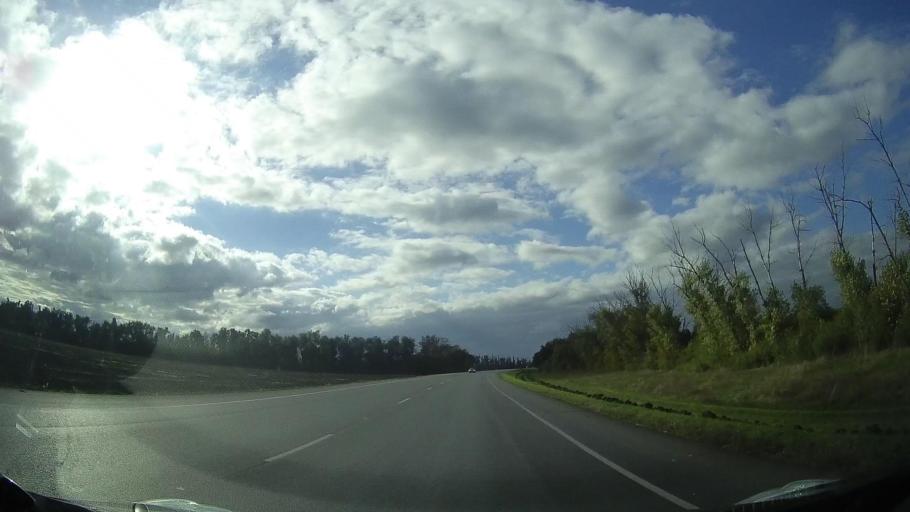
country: RU
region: Rostov
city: Tselina
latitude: 46.5302
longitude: 40.9479
